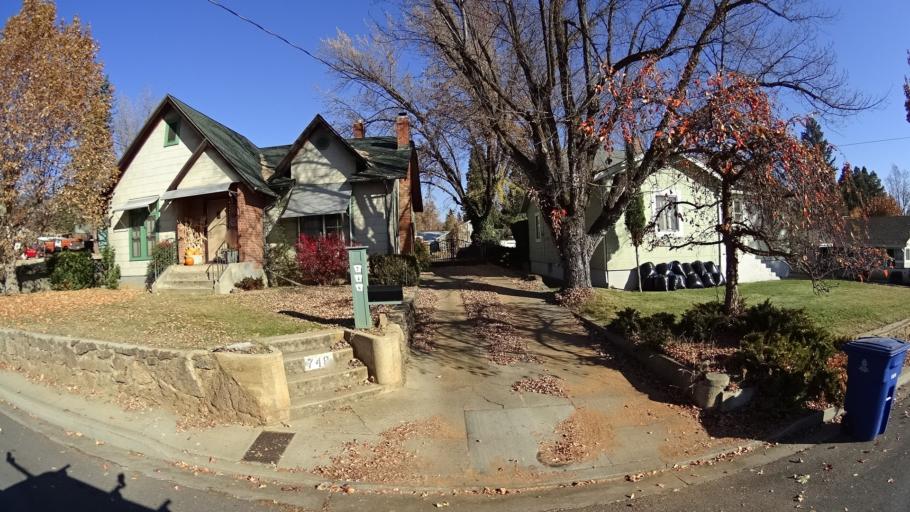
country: US
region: California
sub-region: Siskiyou County
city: Yreka
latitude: 41.7344
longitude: -122.6449
